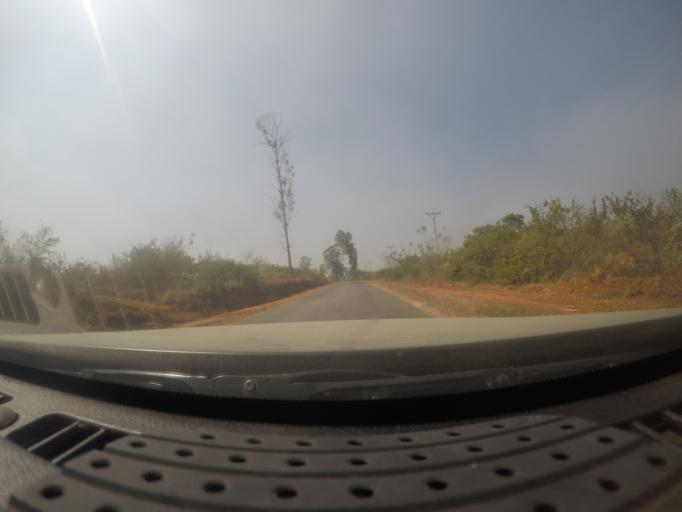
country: MM
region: Mandalay
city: Kyaukse
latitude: 21.1088
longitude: 96.4784
